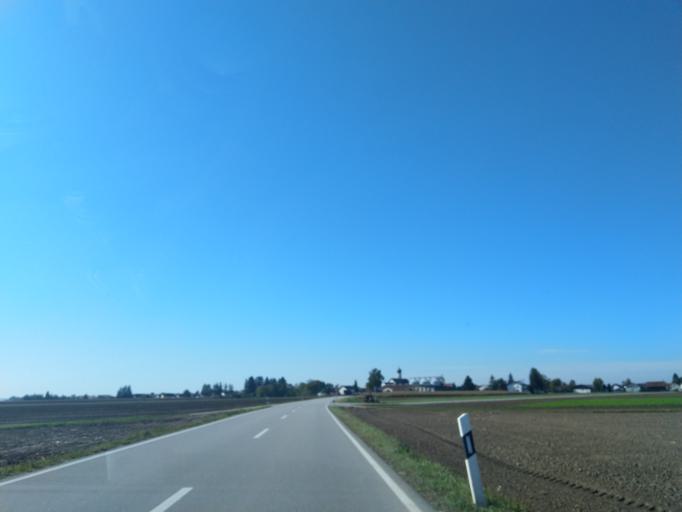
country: DE
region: Bavaria
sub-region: Lower Bavaria
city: Stephansposching
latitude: 48.7878
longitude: 12.7605
